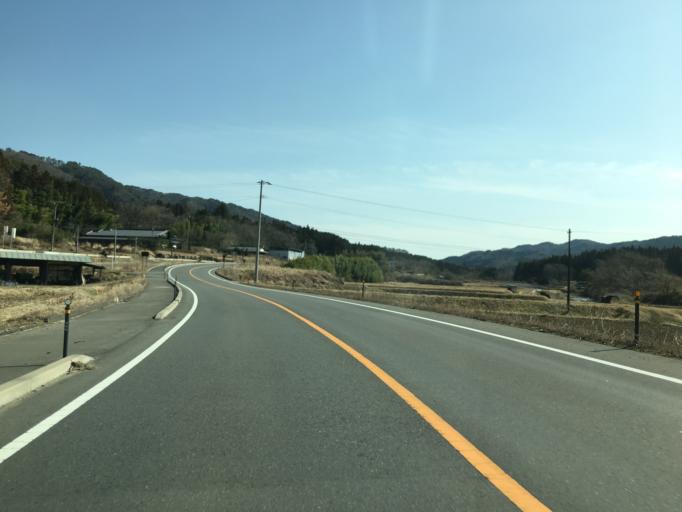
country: JP
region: Ibaraki
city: Daigo
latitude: 36.8313
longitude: 140.4541
